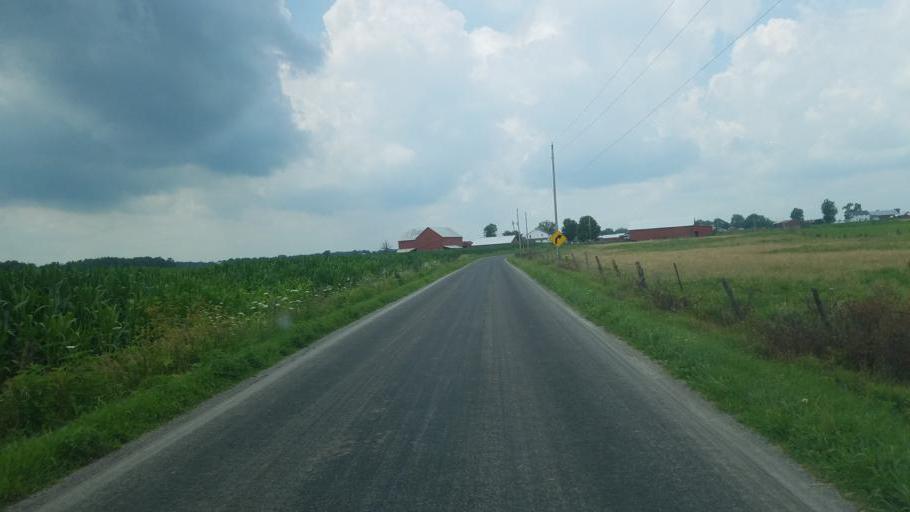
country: US
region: Ohio
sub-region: Hardin County
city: Kenton
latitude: 40.5975
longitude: -83.5451
